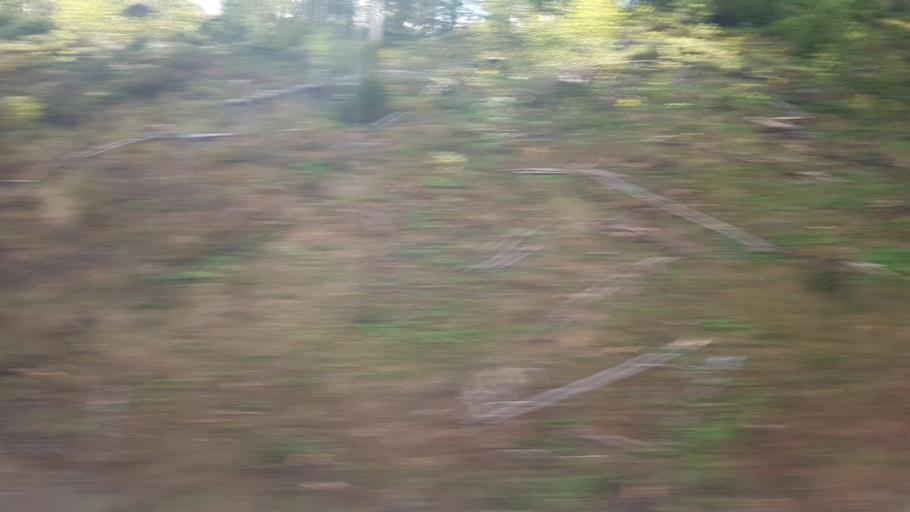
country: NO
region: Sor-Trondelag
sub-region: Rennebu
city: Berkak
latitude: 62.9162
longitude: 10.1408
